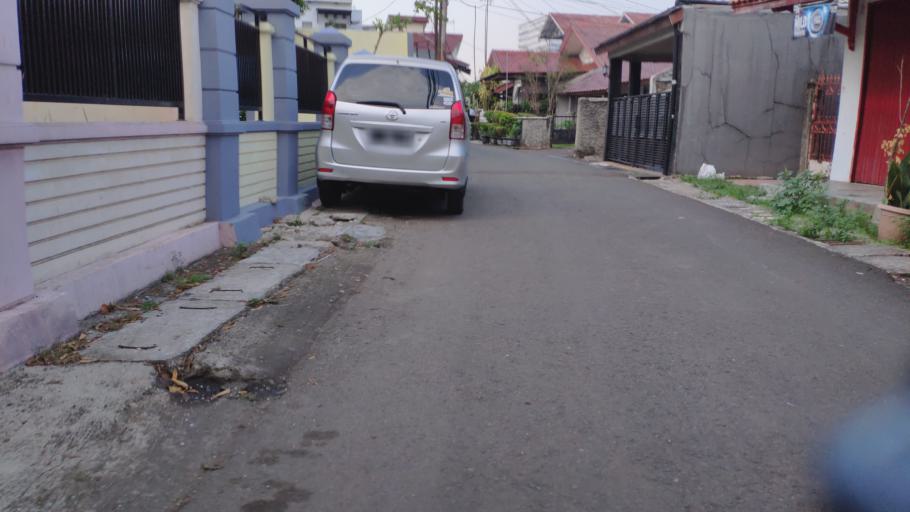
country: ID
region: Jakarta Raya
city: Jakarta
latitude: -6.3010
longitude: 106.8244
